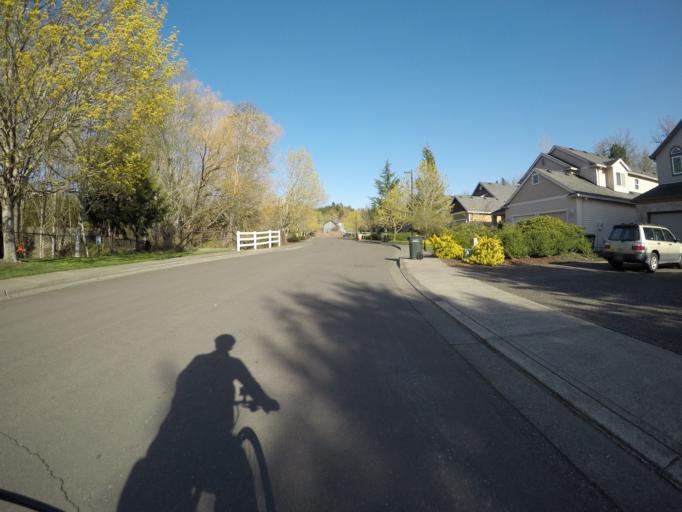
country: US
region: Oregon
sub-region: Washington County
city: Cedar Mill
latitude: 45.5450
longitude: -122.8130
